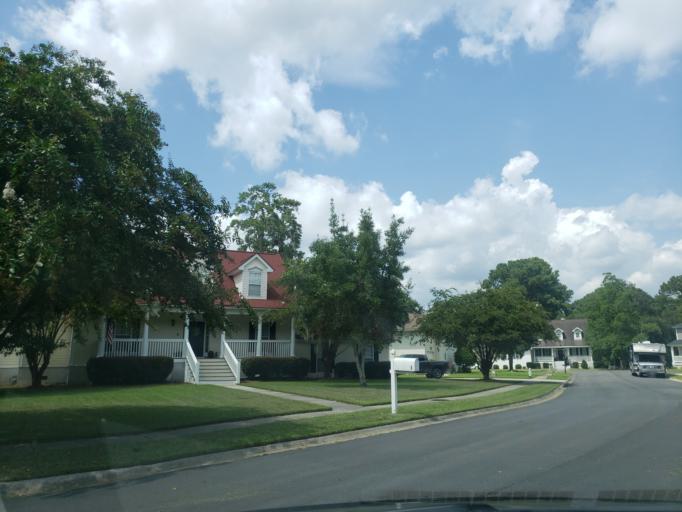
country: US
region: Georgia
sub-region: Chatham County
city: Isle of Hope
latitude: 31.9872
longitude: -81.0478
